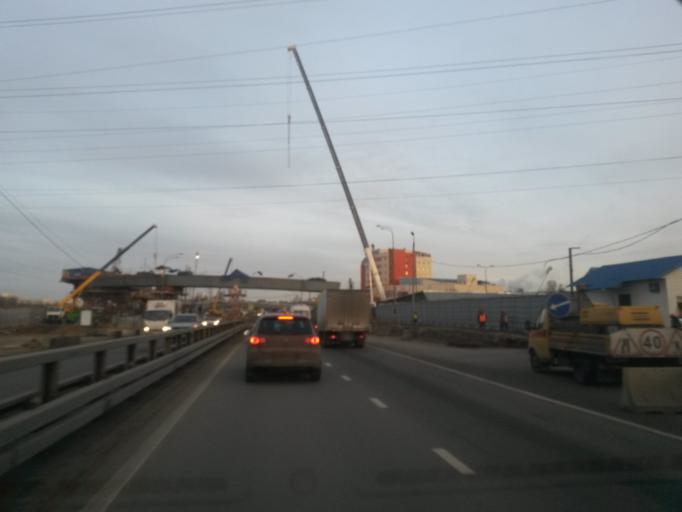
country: RU
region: Moskovskaya
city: Bol'shaya Setun'
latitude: 55.6993
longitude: 37.4222
